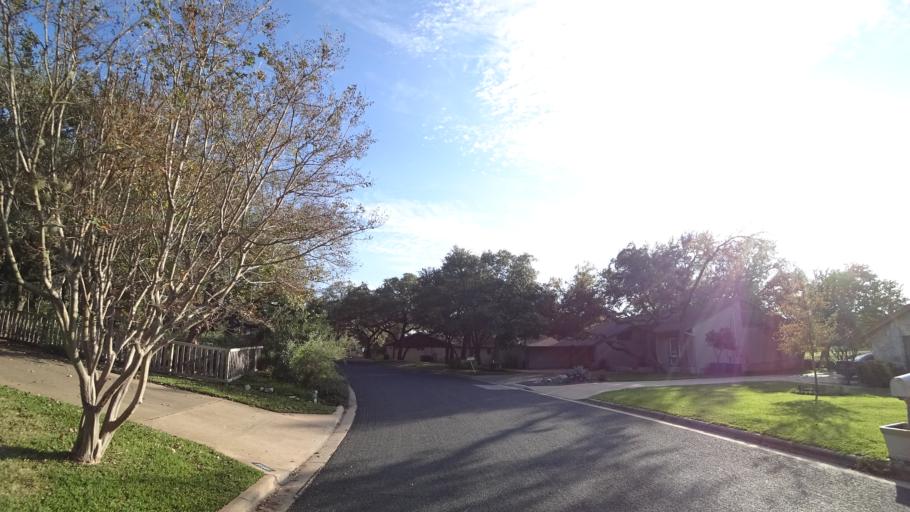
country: US
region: Texas
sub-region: Williamson County
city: Anderson Mill
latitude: 30.4309
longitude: -97.8078
